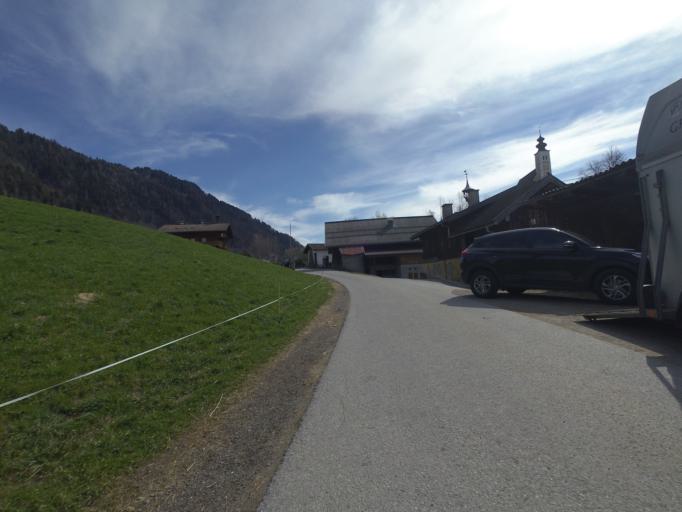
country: AT
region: Salzburg
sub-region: Politischer Bezirk Sankt Johann im Pongau
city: Sankt Veit im Pongau
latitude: 47.3300
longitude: 13.1492
